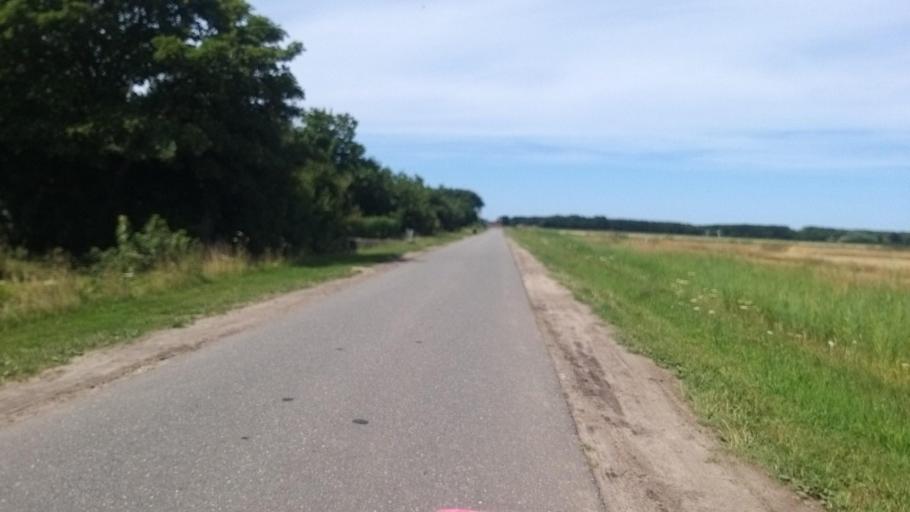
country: NL
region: North Holland
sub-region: Gemeente Texel
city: Den Burg
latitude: 53.1430
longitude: 4.8705
